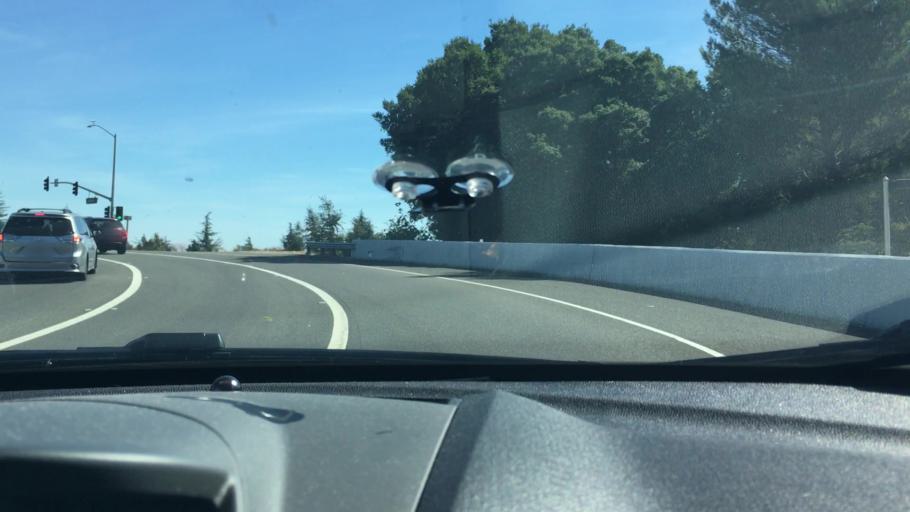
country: US
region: California
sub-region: Alameda County
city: Dublin
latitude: 37.6970
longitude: -121.9358
